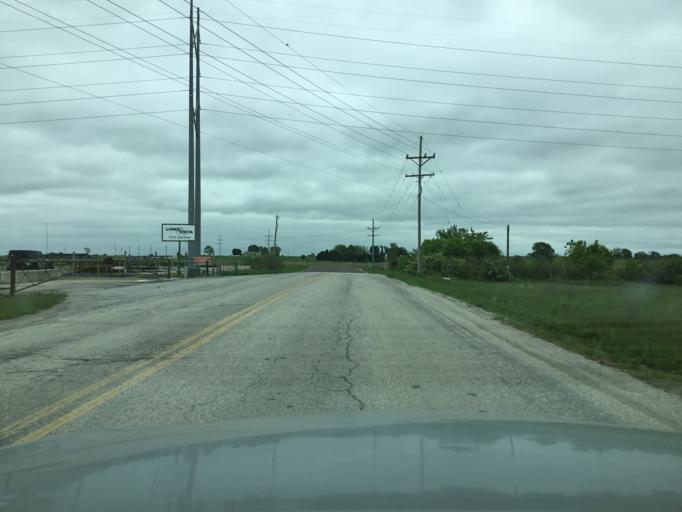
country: US
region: Kansas
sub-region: Franklin County
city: Ottawa
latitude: 38.5793
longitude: -95.2594
